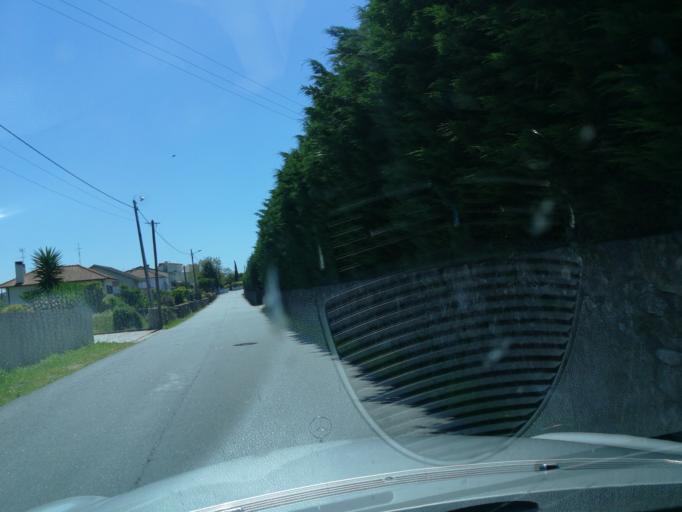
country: PT
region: Viana do Castelo
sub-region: Viana do Castelo
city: Meadela
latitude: 41.7257
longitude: -8.7902
